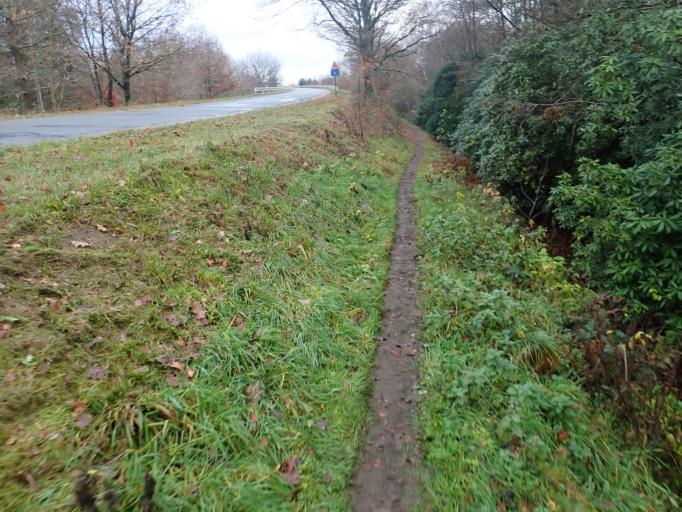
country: BE
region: Flanders
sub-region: Provincie Antwerpen
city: Schoten
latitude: 51.2649
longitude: 4.4845
